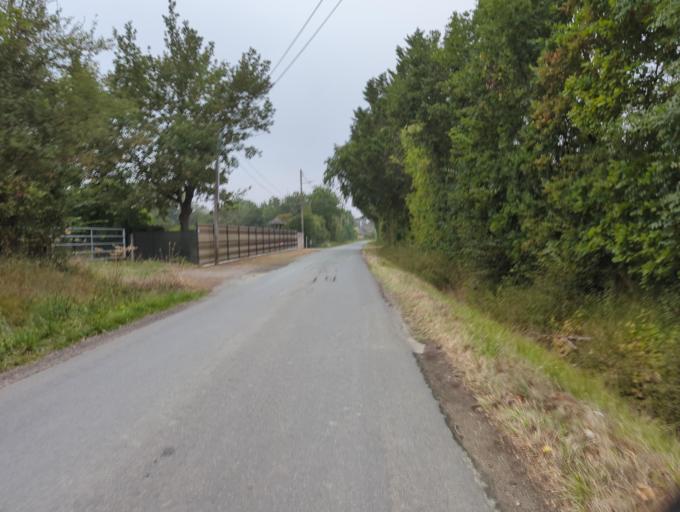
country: FR
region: Pays de la Loire
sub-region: Departement de Maine-et-Loire
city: Trelaze
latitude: 47.4804
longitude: -0.4768
